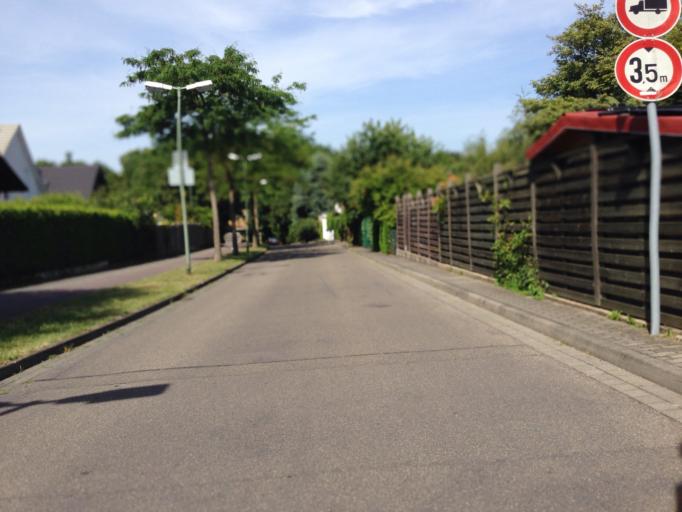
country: DE
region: Hesse
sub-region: Regierungsbezirk Darmstadt
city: Hanau am Main
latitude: 50.1117
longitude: 8.8999
